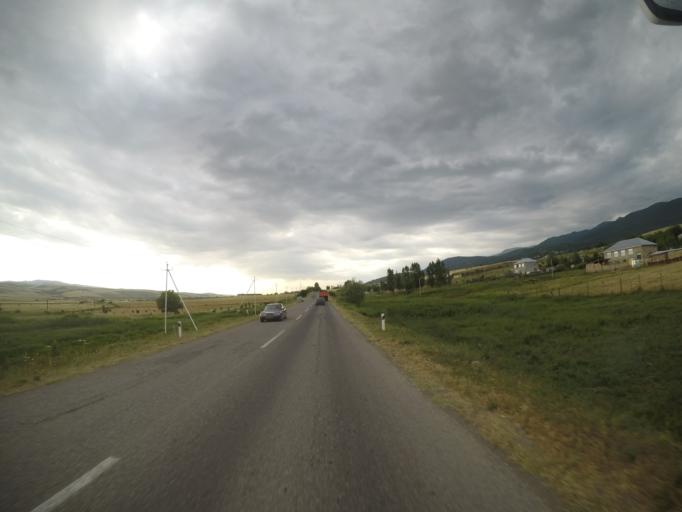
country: AZ
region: Ismayilli
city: Ismayilli
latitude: 40.7397
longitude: 48.2600
